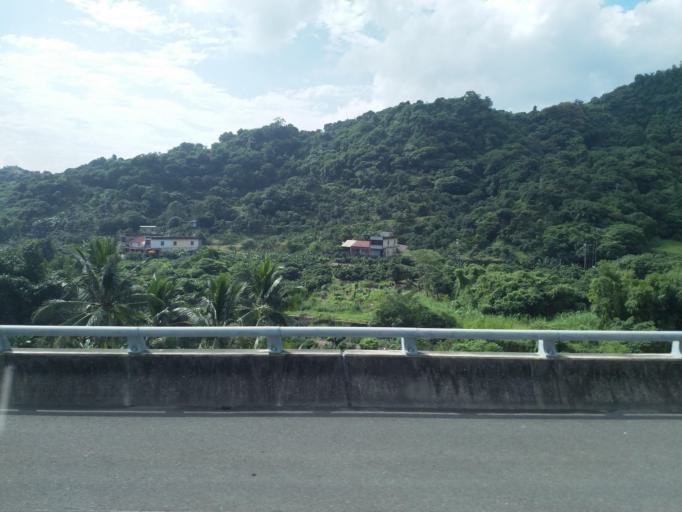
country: TW
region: Taiwan
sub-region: Pingtung
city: Pingtung
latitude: 22.7968
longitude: 120.4446
